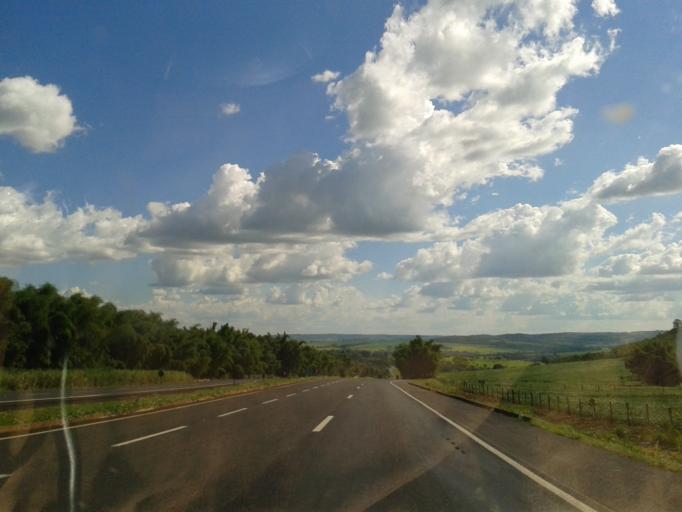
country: BR
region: Goias
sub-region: Goiatuba
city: Goiatuba
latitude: -18.1098
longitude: -49.2775
